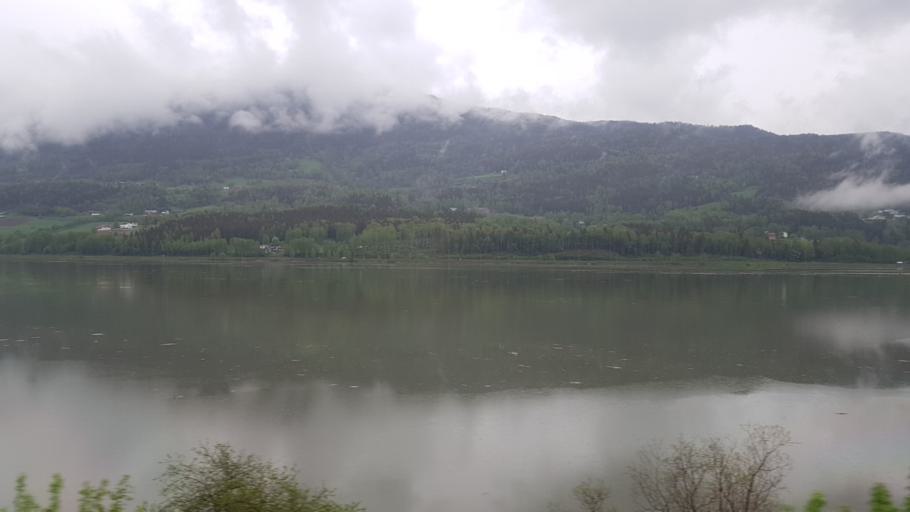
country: NO
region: Oppland
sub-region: Oyer
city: Tretten
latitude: 61.4060
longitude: 10.2421
